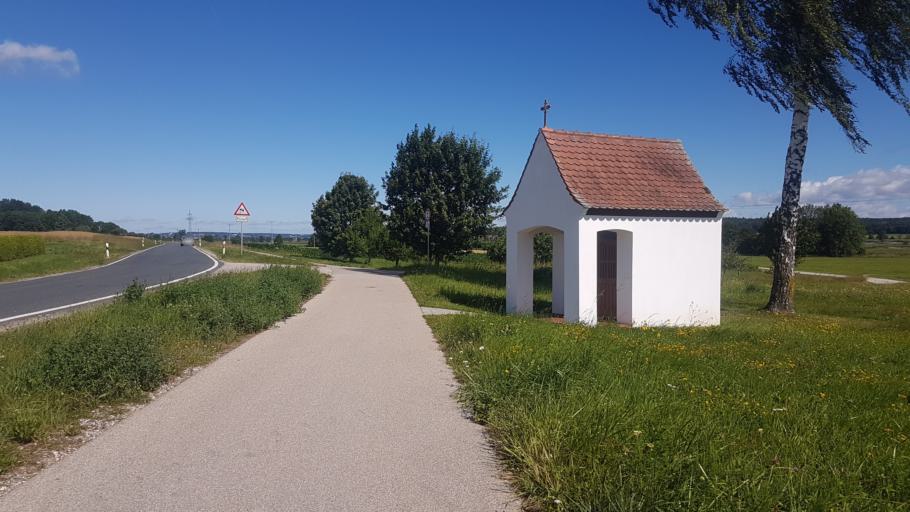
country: DE
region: Bavaria
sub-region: Regierungsbezirk Mittelfranken
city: Burgoberbach
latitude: 49.1939
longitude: 10.5683
